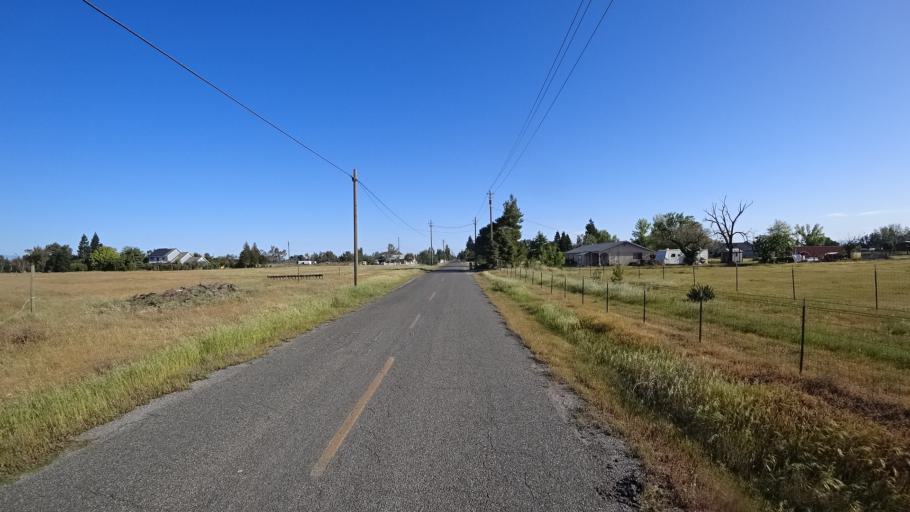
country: US
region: California
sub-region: Glenn County
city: Orland
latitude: 39.7270
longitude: -122.1877
